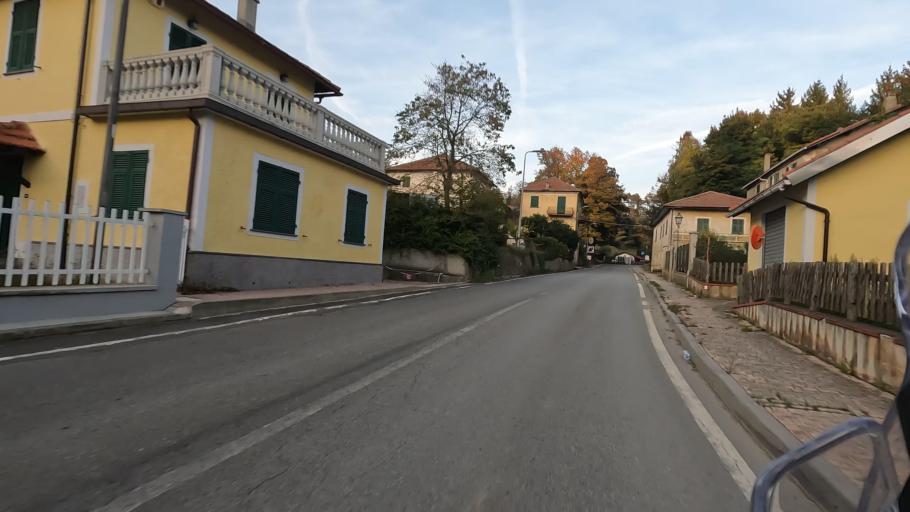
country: IT
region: Liguria
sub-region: Provincia di Savona
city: Osteria dei Cacciatori-Stella
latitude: 44.4303
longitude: 8.4742
